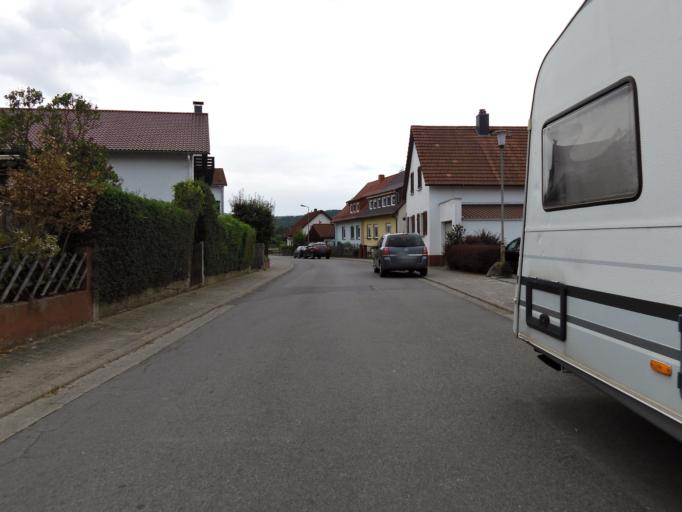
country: DE
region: Hesse
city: Reichelsheim
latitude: 49.7135
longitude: 8.8446
